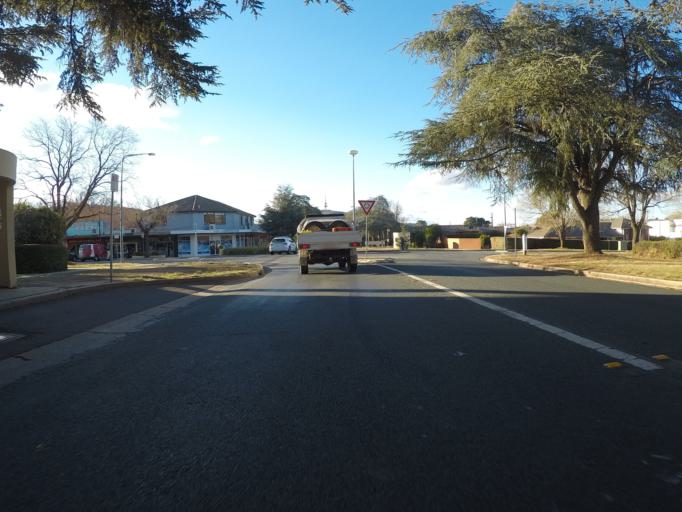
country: AU
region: Australian Capital Territory
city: Forrest
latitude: -35.3080
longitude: 149.0982
